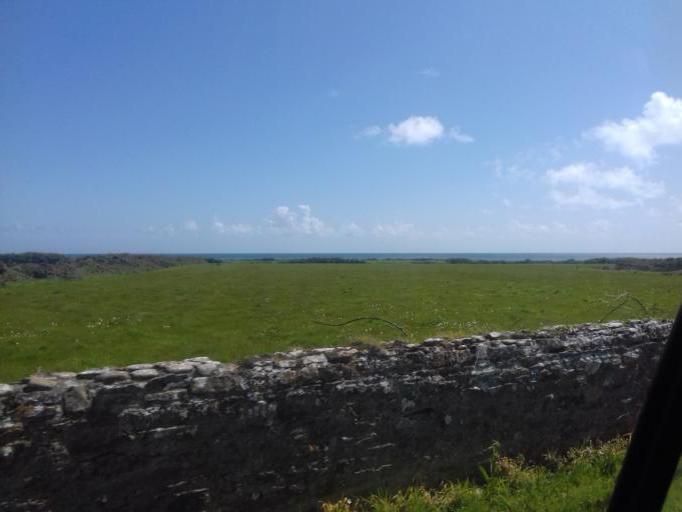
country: IE
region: Munster
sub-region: Waterford
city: Dunmore East
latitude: 52.1531
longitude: -6.8992
